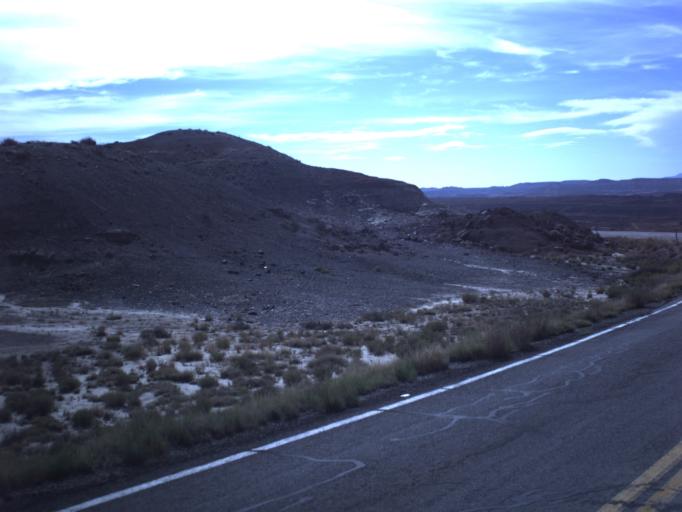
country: US
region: Utah
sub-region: San Juan County
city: Blanding
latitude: 37.3235
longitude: -109.3205
